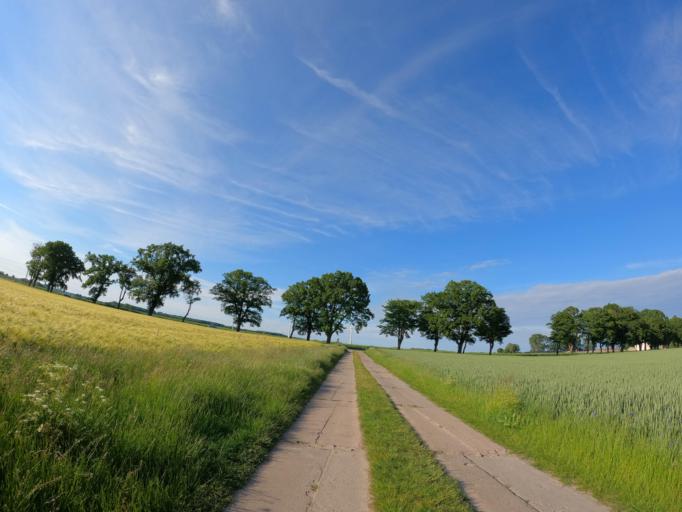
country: DE
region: Mecklenburg-Vorpommern
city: Preetz
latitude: 54.3477
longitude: 13.0024
